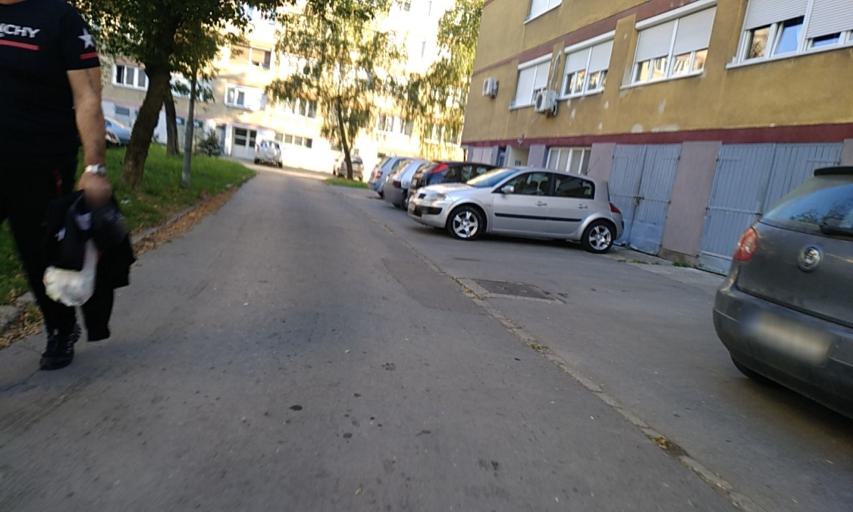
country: BA
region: Republika Srpska
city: Mejdan - Obilicevo
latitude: 44.7605
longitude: 17.1938
